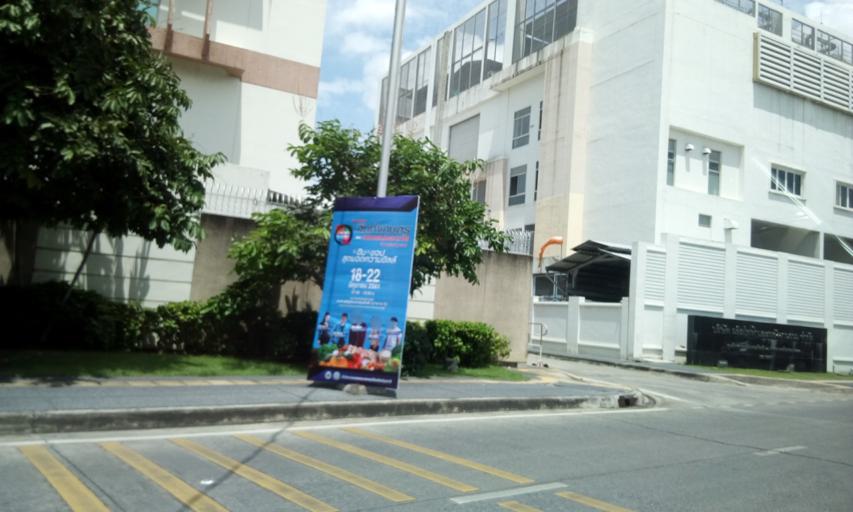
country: TH
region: Bangkok
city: Lak Si
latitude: 13.8846
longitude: 100.5630
